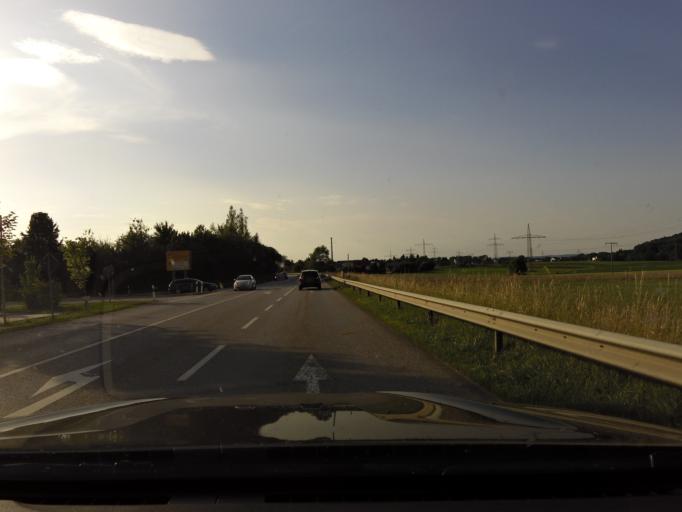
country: DE
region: Bavaria
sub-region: Upper Bavaria
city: Burgkirchen an der Alz
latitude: 48.1583
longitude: 12.7429
